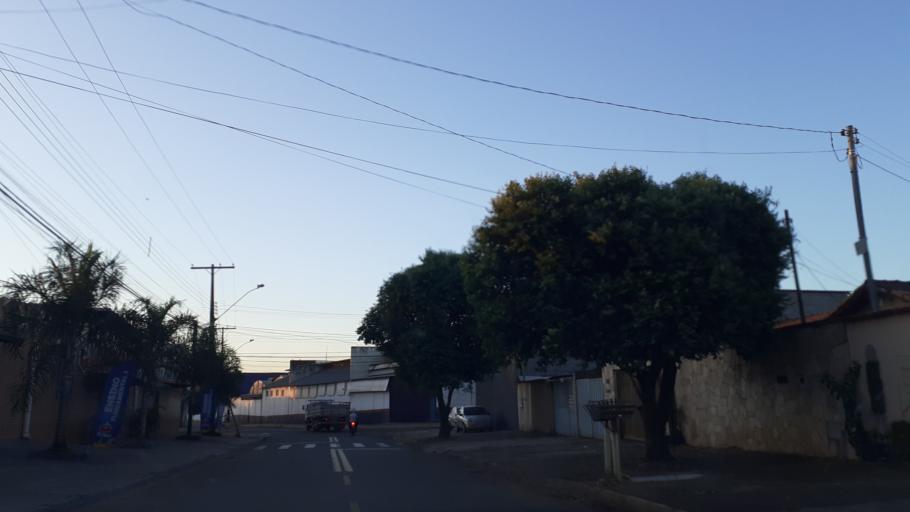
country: BR
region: Goias
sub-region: Goiania
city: Goiania
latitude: -16.7010
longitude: -49.3287
